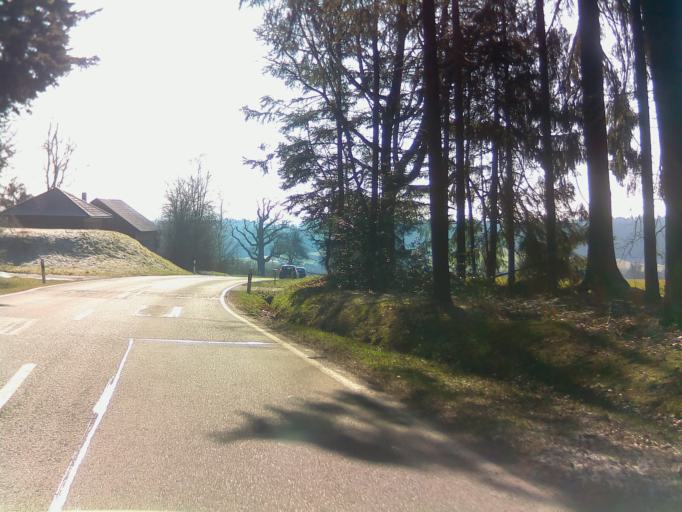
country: DE
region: Baden-Wuerttemberg
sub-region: Karlsruhe Region
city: Neuweiler
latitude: 48.6832
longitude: 8.6111
